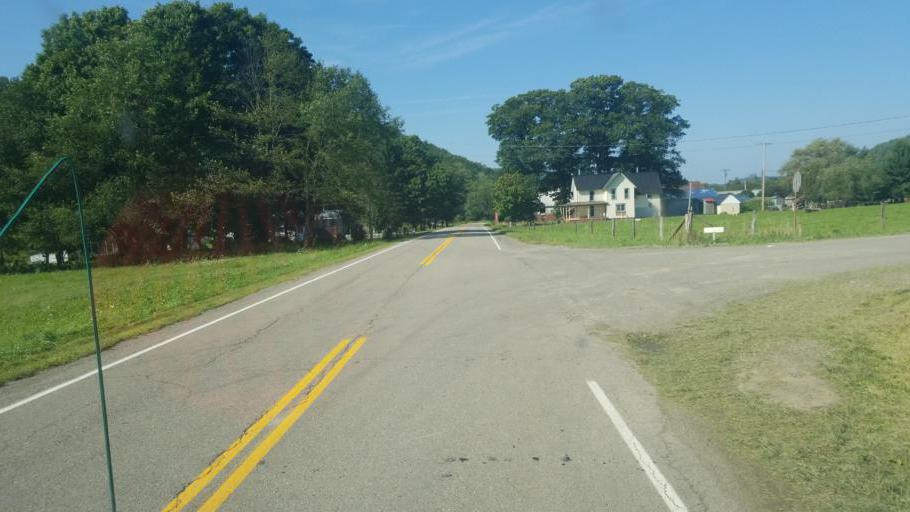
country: US
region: New York
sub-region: Allegany County
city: Wellsville
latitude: 42.0285
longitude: -77.9414
